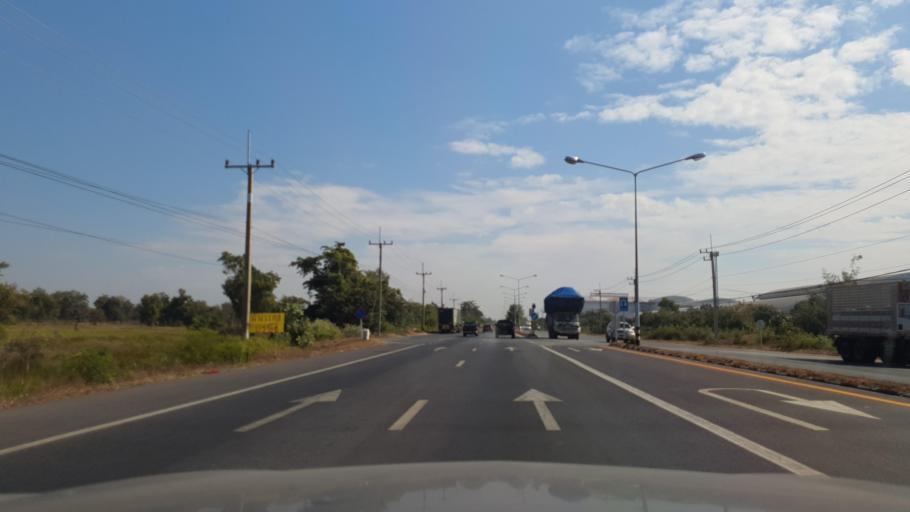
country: TH
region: Maha Sarakham
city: Kantharawichai
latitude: 16.3828
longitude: 103.2171
